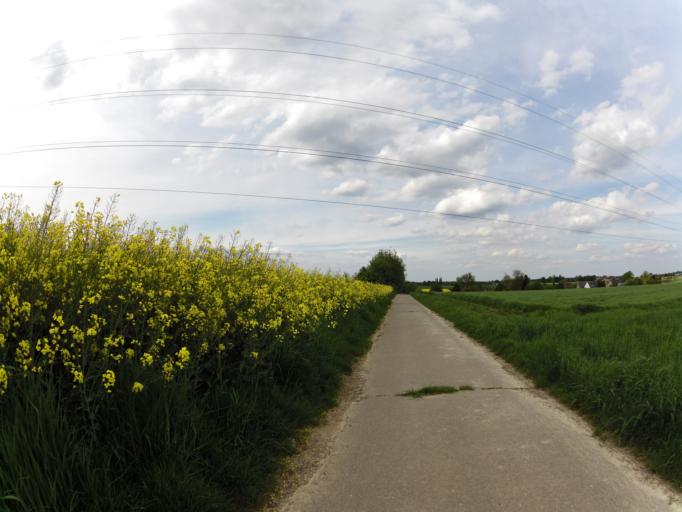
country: DE
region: North Rhine-Westphalia
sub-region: Regierungsbezirk Koln
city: Herzogenrath
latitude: 50.8882
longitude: 6.0917
